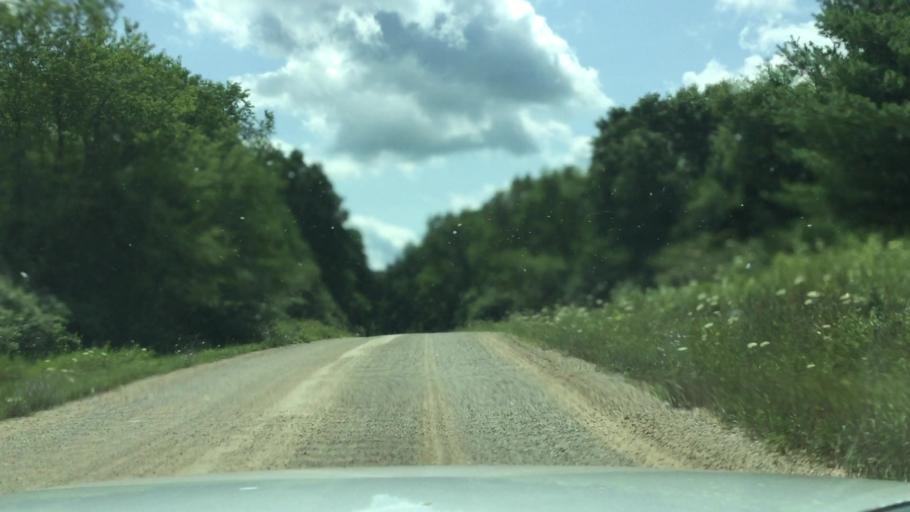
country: US
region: Michigan
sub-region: Ionia County
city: Belding
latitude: 43.1163
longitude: -85.2095
